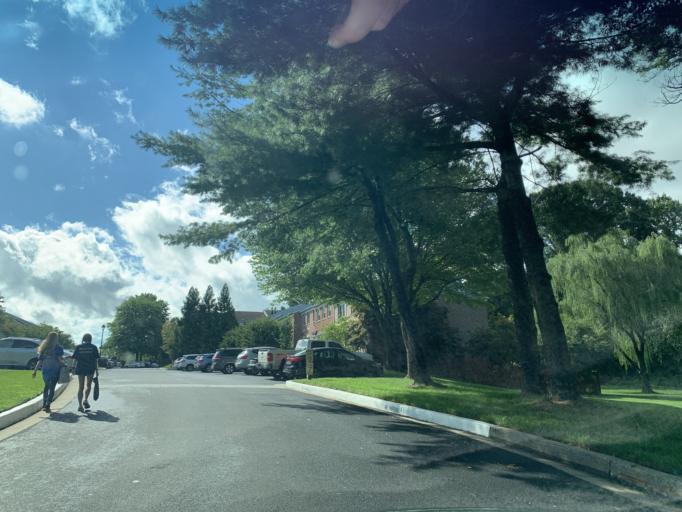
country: US
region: Maryland
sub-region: Baltimore County
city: Timonium
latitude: 39.4478
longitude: -76.6109
